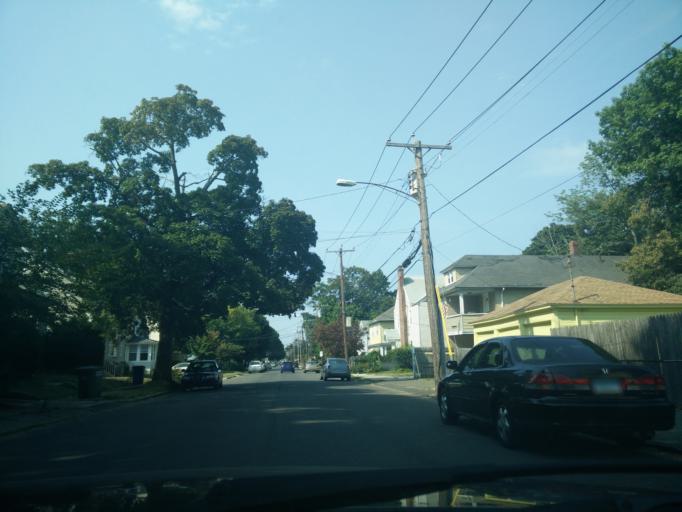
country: US
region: Connecticut
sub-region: Fairfield County
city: Trumbull
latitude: 41.2100
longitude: -73.2093
